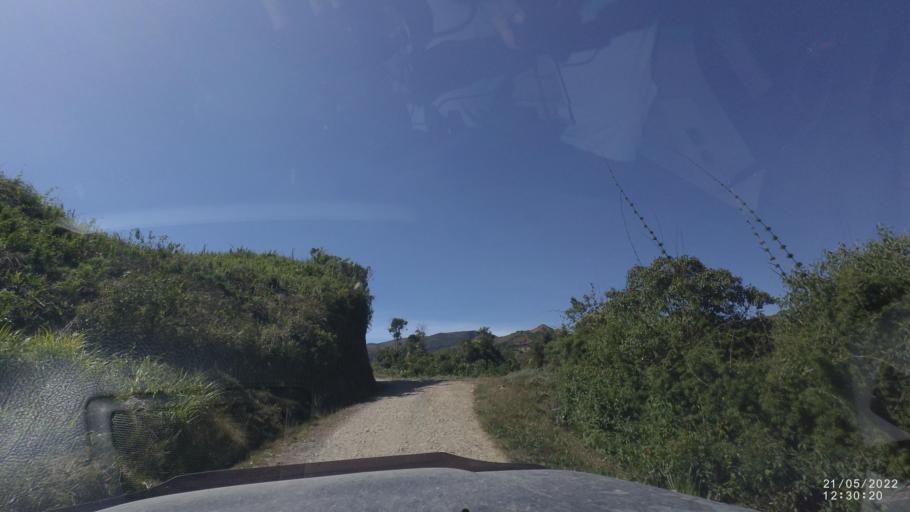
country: BO
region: Cochabamba
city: Colomi
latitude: -17.2152
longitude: -65.9135
